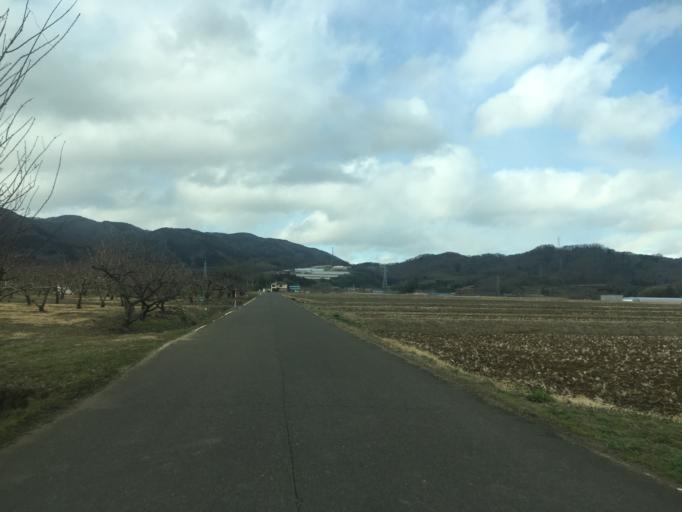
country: JP
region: Fukushima
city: Yanagawamachi-saiwaicho
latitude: 37.8824
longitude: 140.5820
